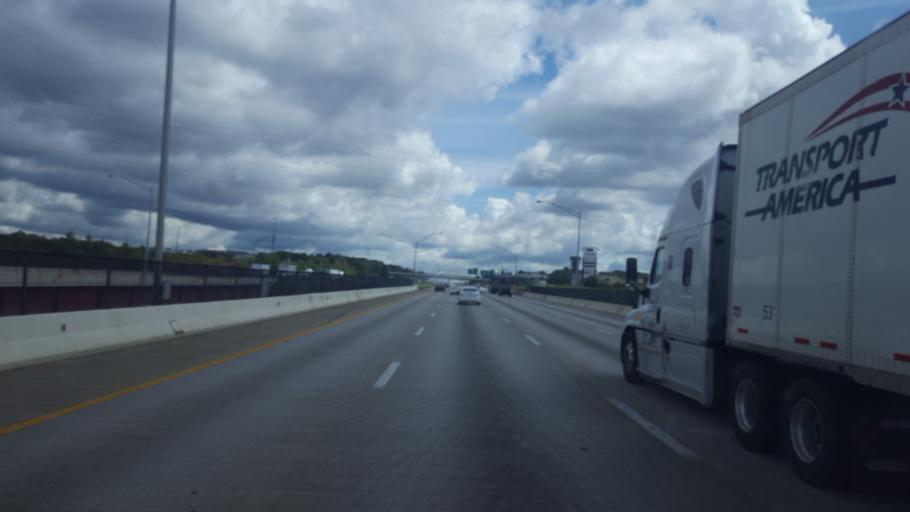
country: US
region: Ohio
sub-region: Cuyahoga County
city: Garfield Heights
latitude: 41.4100
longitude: -81.6238
